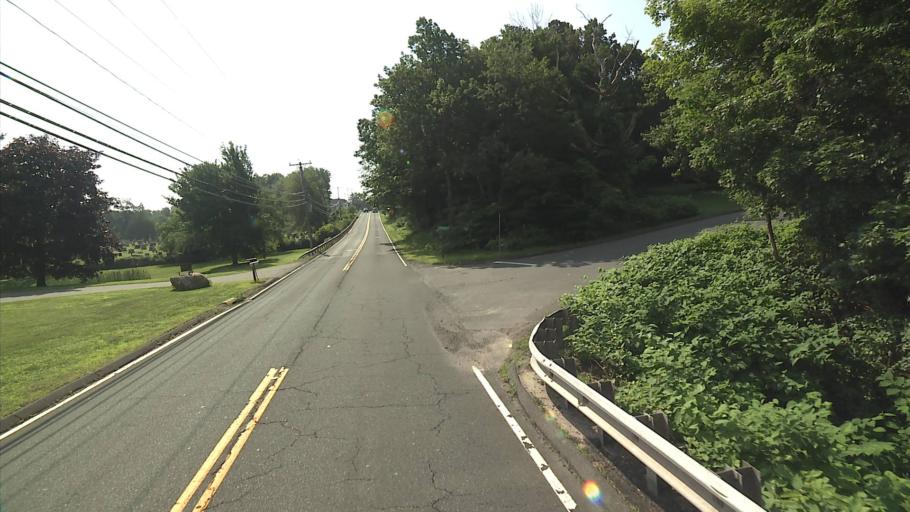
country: US
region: Connecticut
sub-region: New Haven County
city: Wolcott
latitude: 41.6027
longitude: -72.9781
